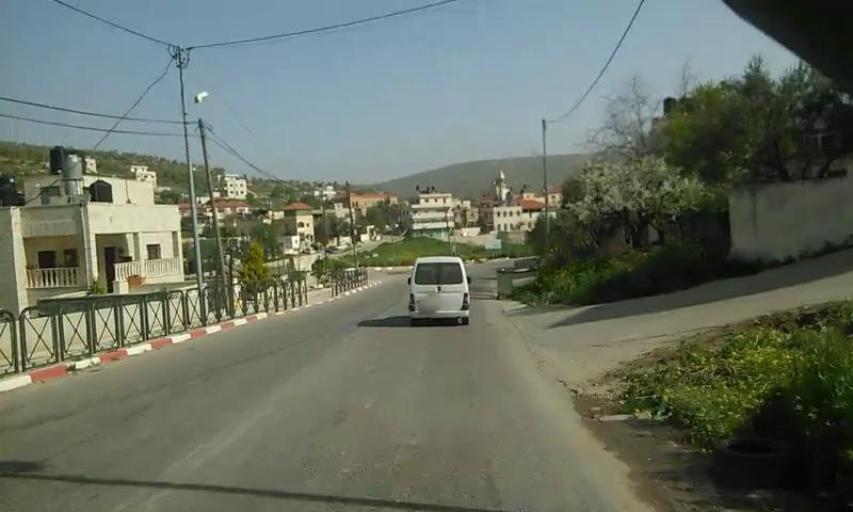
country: PS
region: West Bank
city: Dura al Qar`
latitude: 31.9705
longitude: 35.2280
